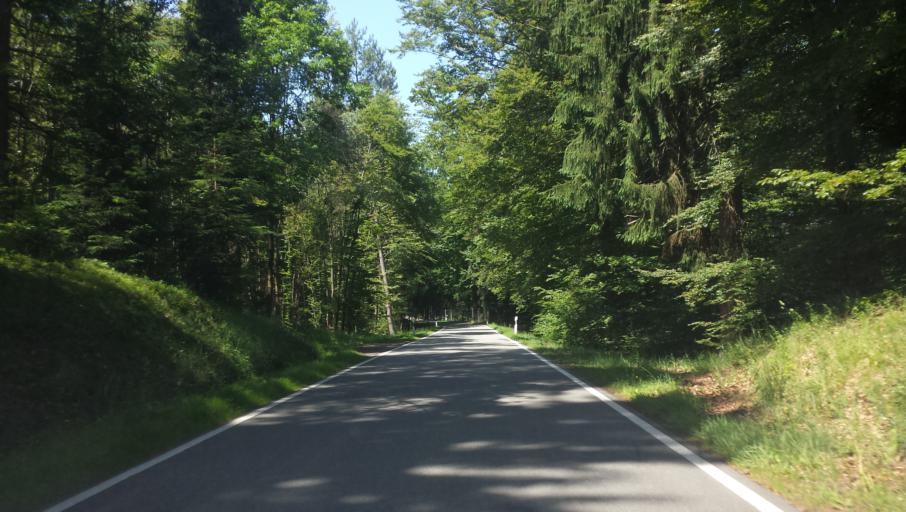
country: DE
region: Rheinland-Pfalz
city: Trippstadt
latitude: 49.3343
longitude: 7.7975
